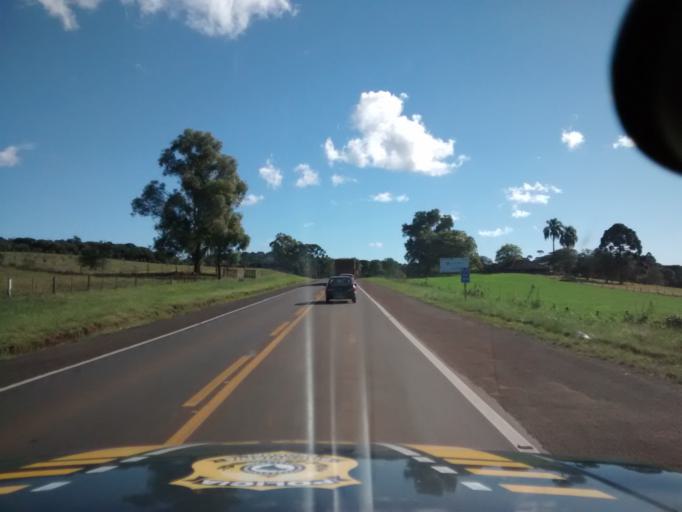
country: BR
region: Rio Grande do Sul
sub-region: Lagoa Vermelha
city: Lagoa Vermelha
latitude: -28.2938
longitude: -51.4422
